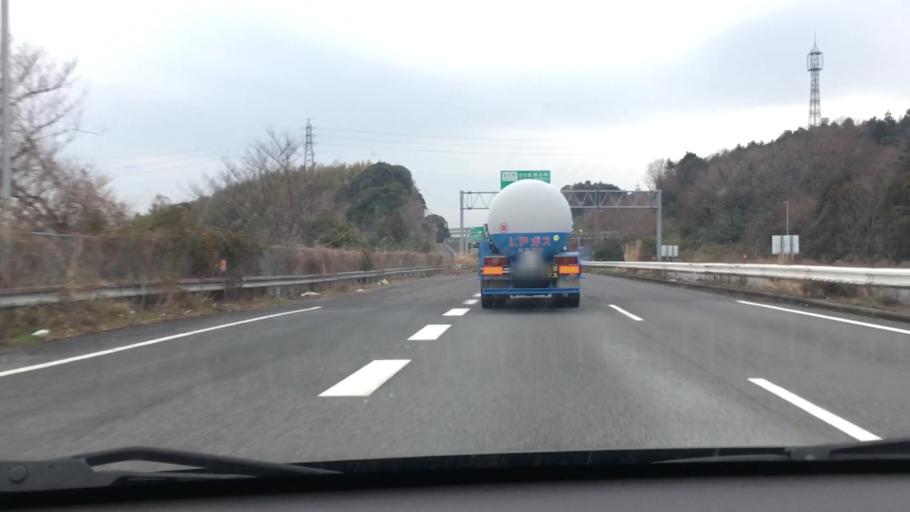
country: JP
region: Mie
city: Kameyama
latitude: 34.8457
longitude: 136.4106
